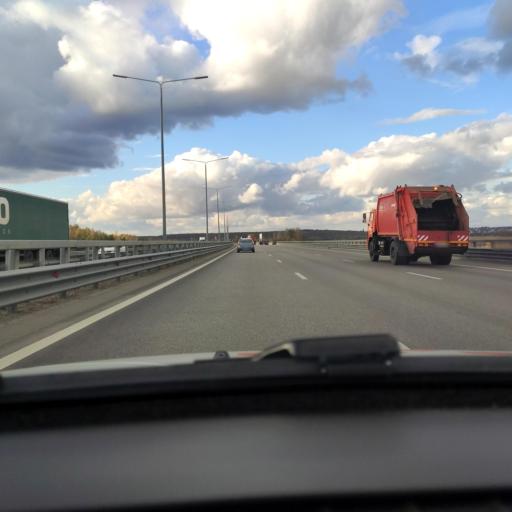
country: RU
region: Voronezj
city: Somovo
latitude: 51.7819
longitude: 39.2931
